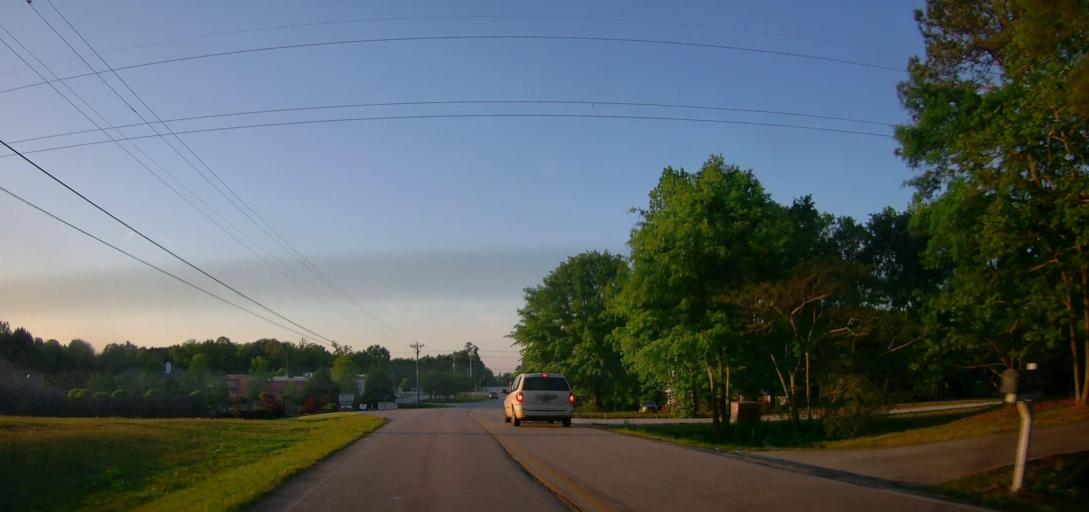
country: US
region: Georgia
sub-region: Henry County
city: McDonough
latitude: 33.4265
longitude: -84.0907
